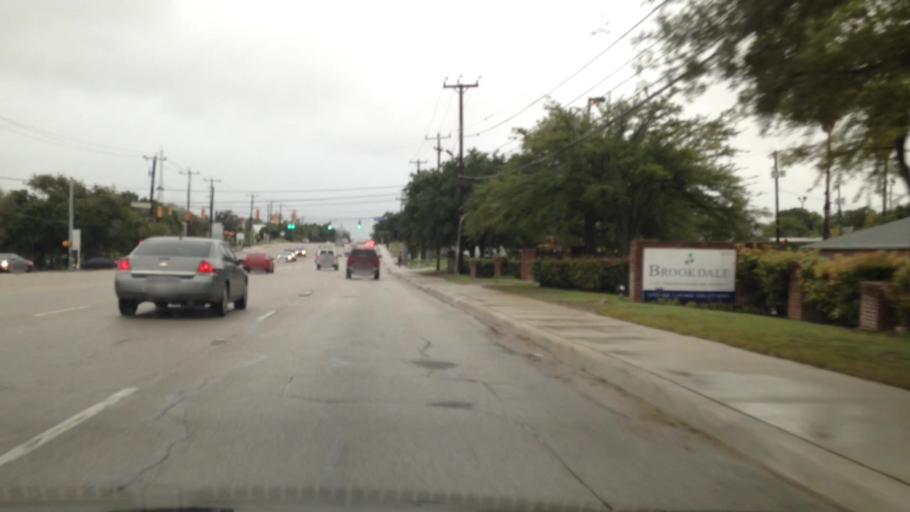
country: US
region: Texas
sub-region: Bexar County
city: Balcones Heights
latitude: 29.5270
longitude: -98.5755
